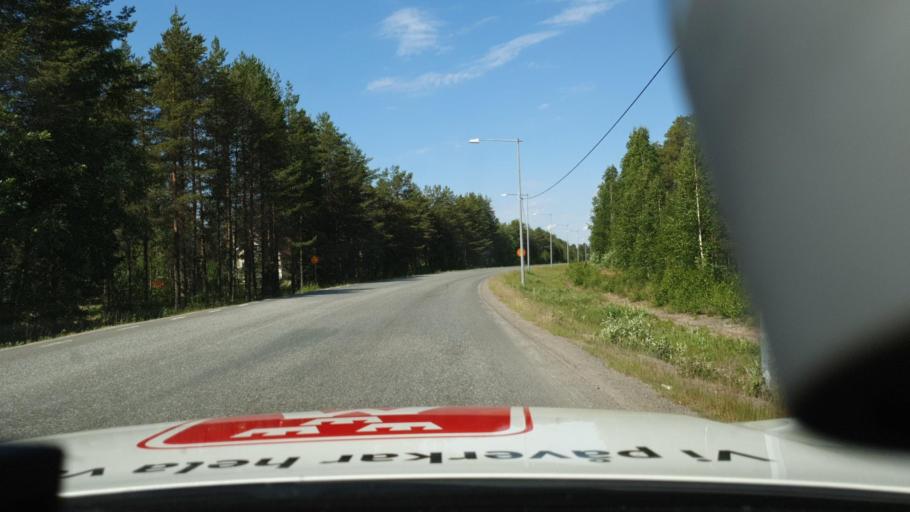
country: SE
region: Norrbotten
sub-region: Kalix Kommun
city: Kalix
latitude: 65.8639
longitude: 23.1379
